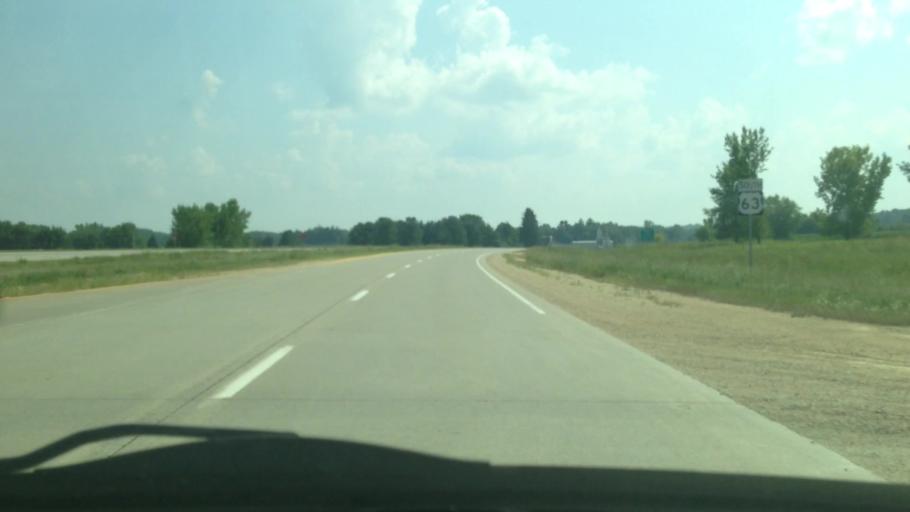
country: US
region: Iowa
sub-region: Bremer County
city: Denver
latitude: 42.6858
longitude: -92.3377
